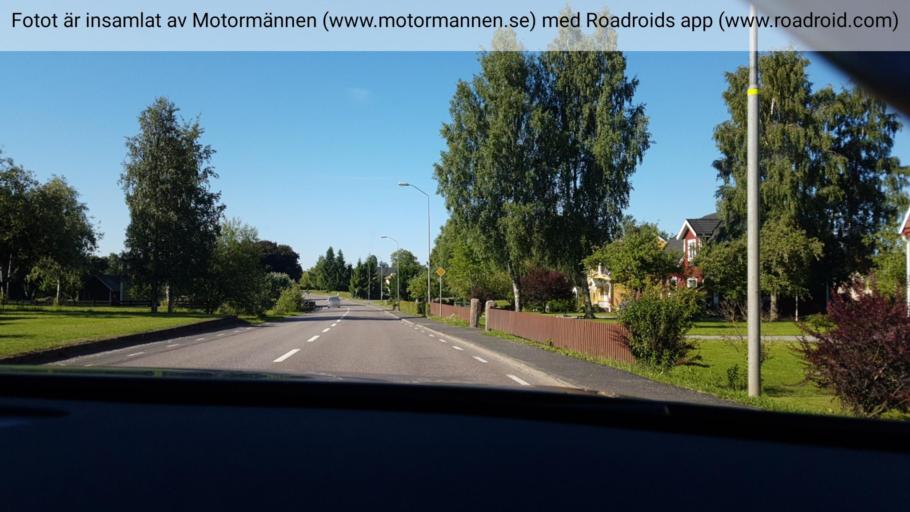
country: SE
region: Vaestra Goetaland
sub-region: Falkopings Kommun
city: Falkoeping
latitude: 58.0847
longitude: 13.5173
